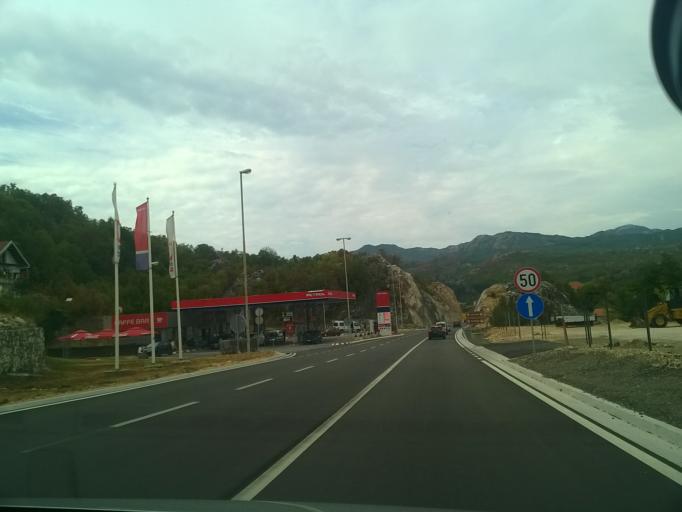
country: ME
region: Cetinje
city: Cetinje
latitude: 42.3880
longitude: 18.9340
